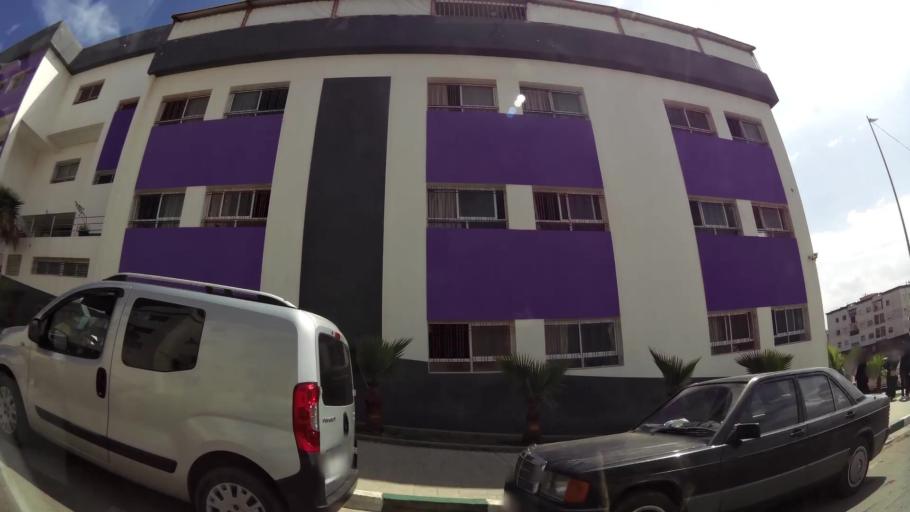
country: MA
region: Rabat-Sale-Zemmour-Zaer
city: Sale
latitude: 34.0773
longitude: -6.7941
